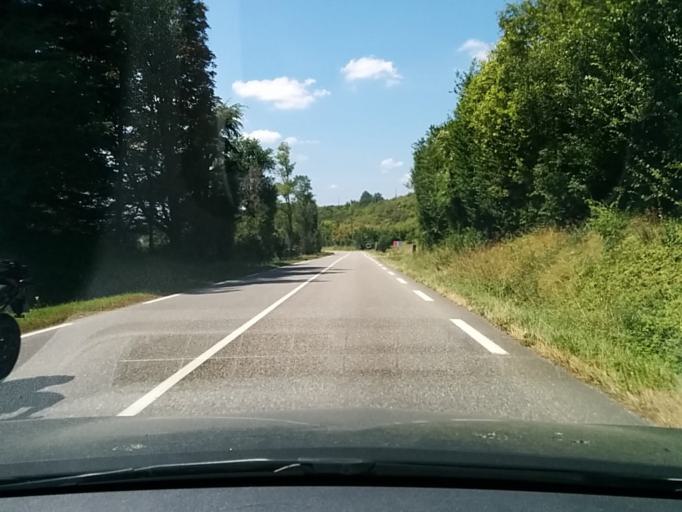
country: FR
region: Midi-Pyrenees
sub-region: Departement du Gers
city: Vic-Fezensac
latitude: 43.7482
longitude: 0.3368
